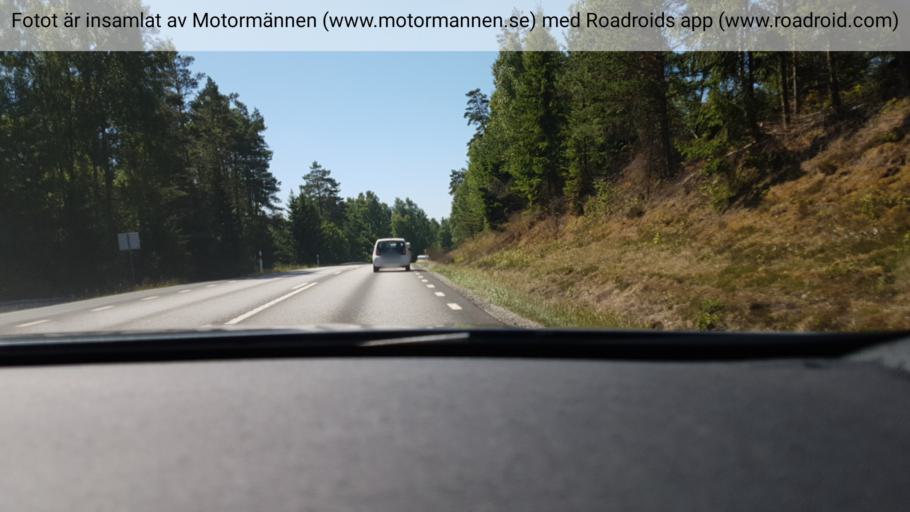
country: SE
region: Joenkoeping
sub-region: Gnosjo Kommun
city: Gnosjoe
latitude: 57.5230
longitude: 13.6846
